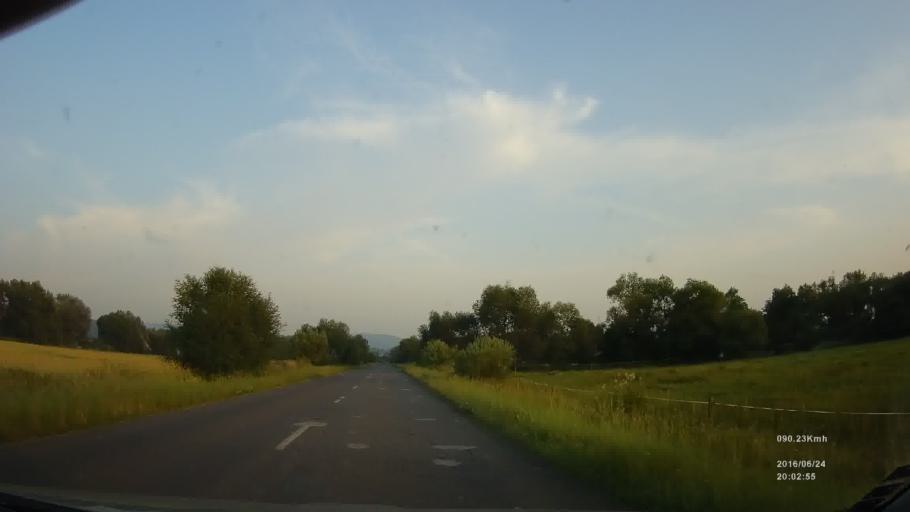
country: SK
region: Banskobystricky
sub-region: Okres Banska Bystrica
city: Zvolen
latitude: 48.6225
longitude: 19.1273
